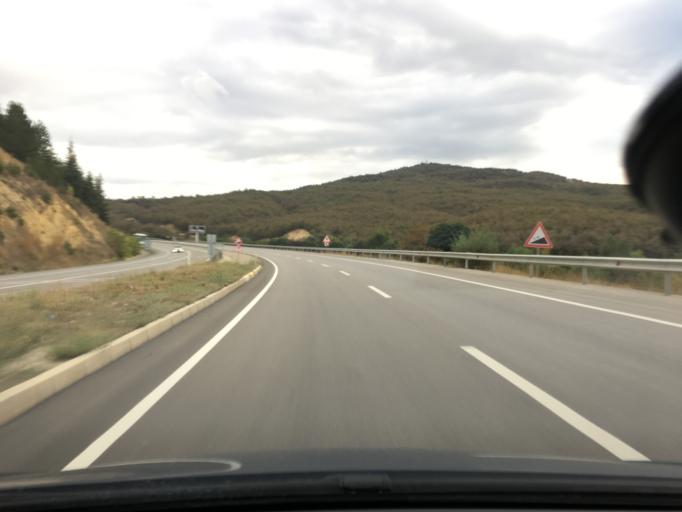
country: TR
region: Afyonkarahisar
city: Sincanli
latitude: 38.7086
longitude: 30.3185
